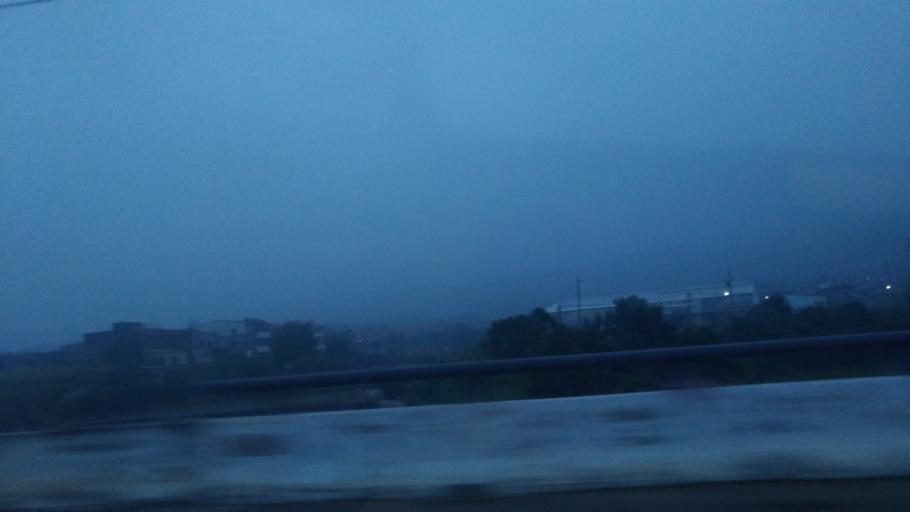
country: TW
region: Taiwan
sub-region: Miaoli
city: Miaoli
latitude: 24.5431
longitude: 120.6972
